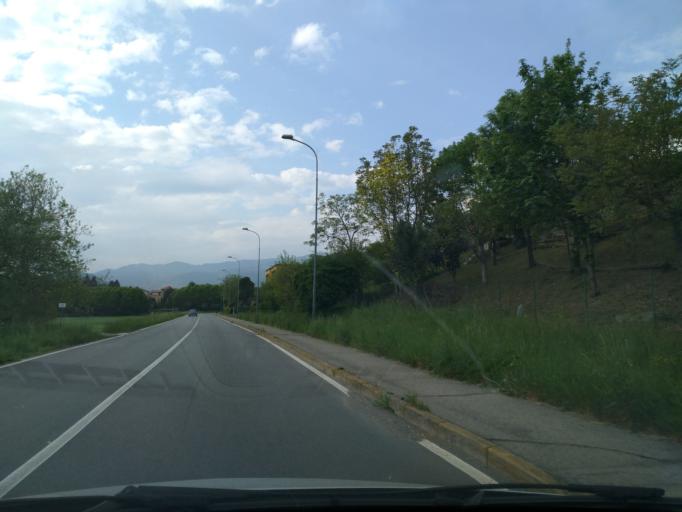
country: IT
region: Lombardy
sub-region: Provincia di Como
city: Alzate Brianza
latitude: 45.7650
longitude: 9.1812
